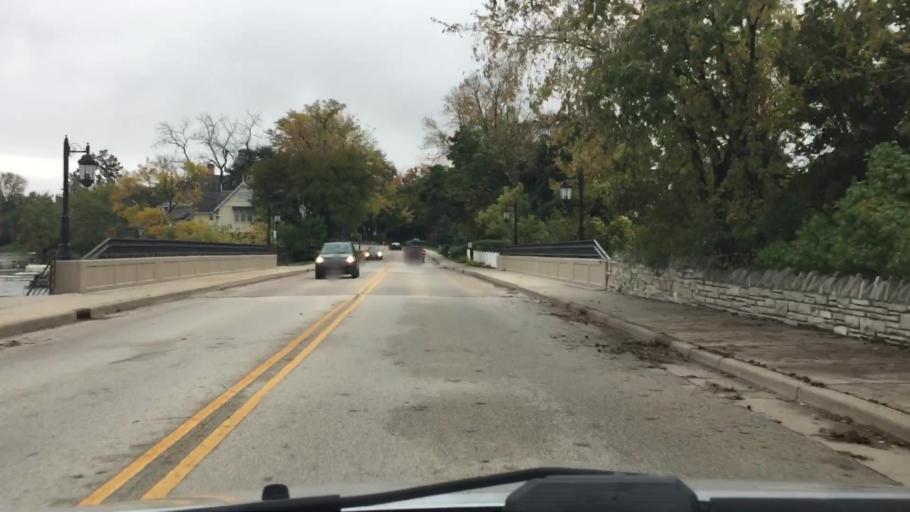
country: US
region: Wisconsin
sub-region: Waukesha County
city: Oconomowoc
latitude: 43.1171
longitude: -88.4995
